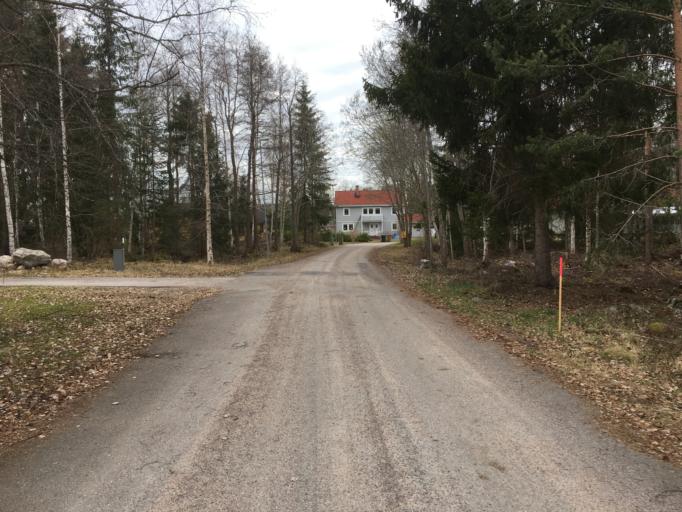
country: SE
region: Gaevleborg
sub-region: Hofors Kommun
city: Hofors
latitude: 60.5144
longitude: 16.4681
